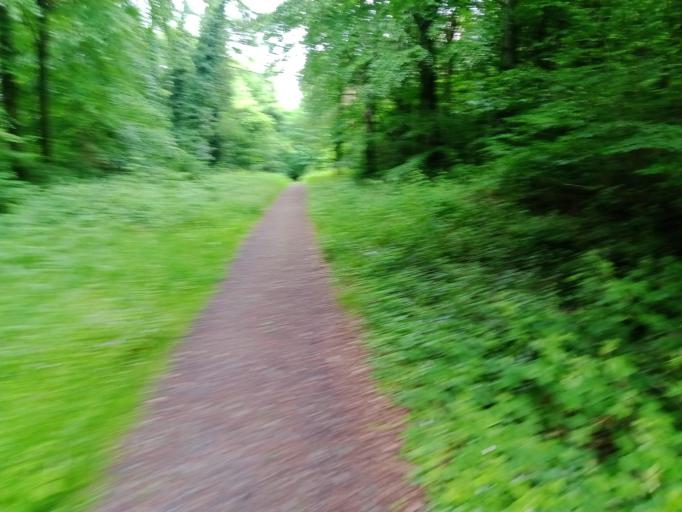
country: IE
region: Leinster
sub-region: Laois
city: Stradbally
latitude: 53.0024
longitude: -7.1228
